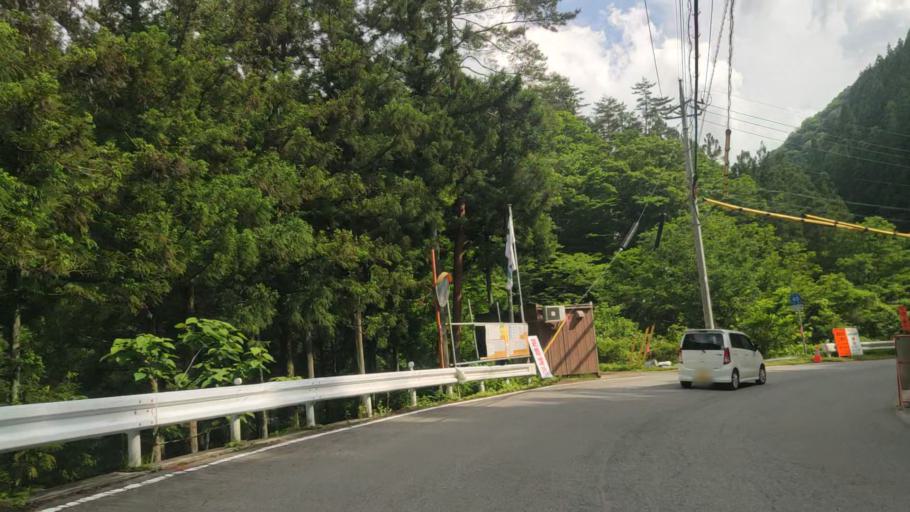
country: JP
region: Gunma
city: Tomioka
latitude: 36.1041
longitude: 138.7178
